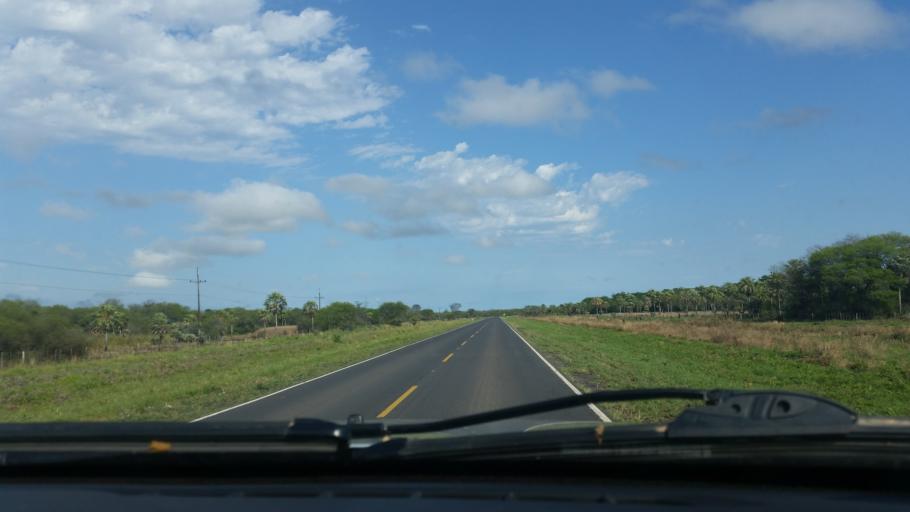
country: PY
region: Presidente Hayes
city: Benjamin Aceval
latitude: -24.9095
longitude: -57.6359
